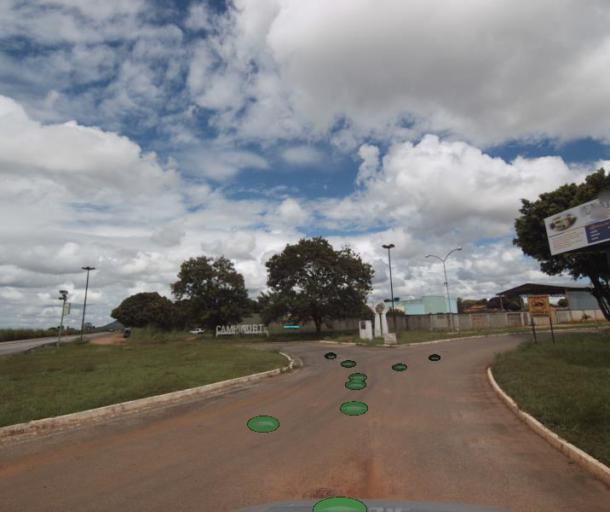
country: BR
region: Goias
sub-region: Uruacu
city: Uruacu
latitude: -14.3335
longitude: -49.1545
